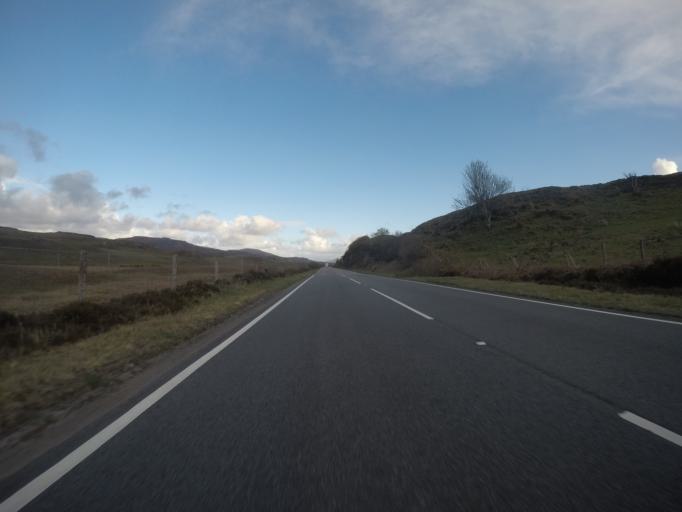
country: GB
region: Scotland
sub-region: Highland
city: Isle of Skye
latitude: 57.5101
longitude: -6.3394
